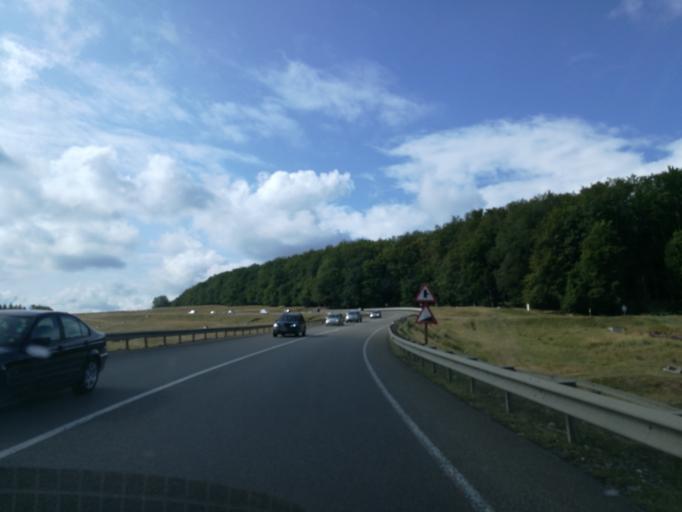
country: RO
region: Suceava
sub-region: Comuna Ilisesti
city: Ilisesti
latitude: 47.5975
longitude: 26.0211
